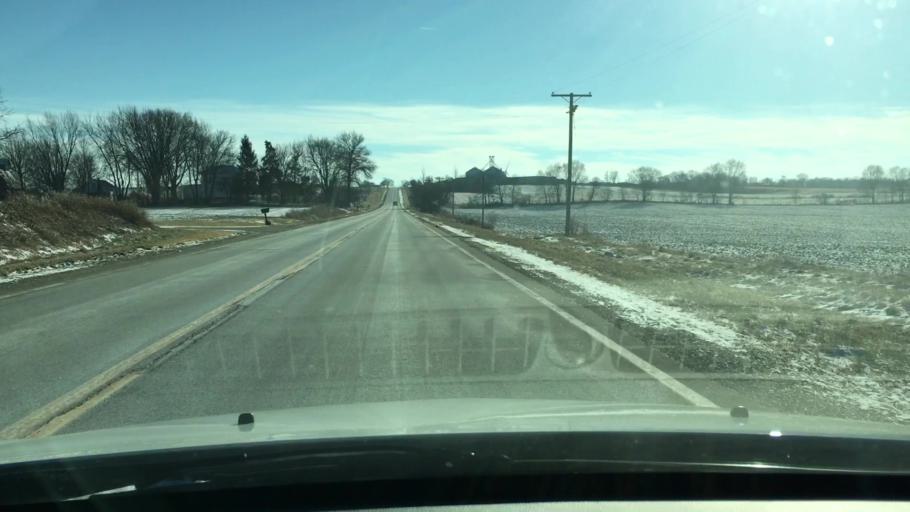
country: US
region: Illinois
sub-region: LaSalle County
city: Mendota
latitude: 41.7269
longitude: -89.0838
